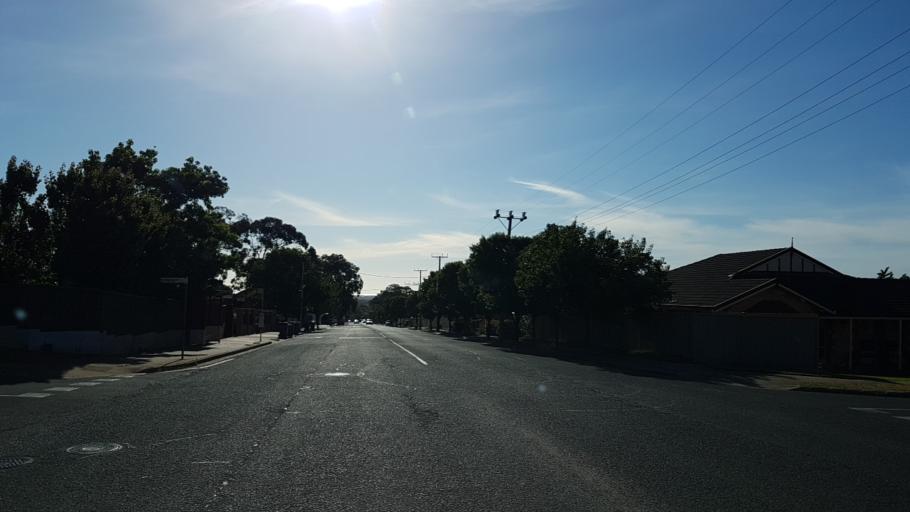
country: AU
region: South Australia
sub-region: Burnside
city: Wattle Park
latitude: -34.9024
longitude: 138.6815
